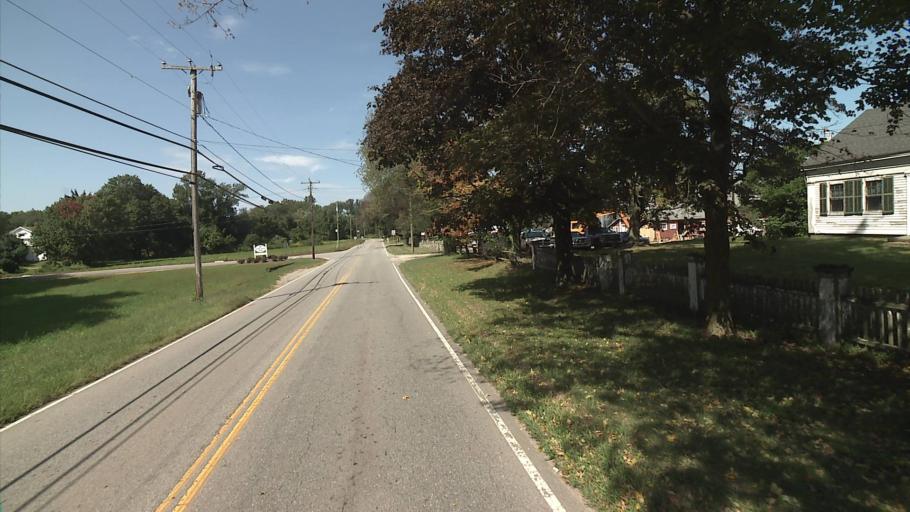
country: US
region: Connecticut
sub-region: Windham County
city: South Windham
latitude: 41.6266
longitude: -72.1984
